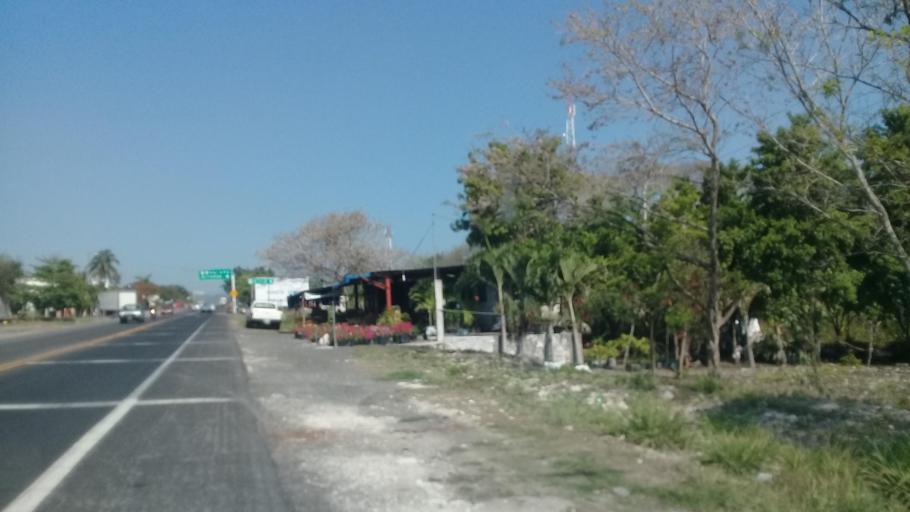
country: MX
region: Veracruz
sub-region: Emiliano Zapata
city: Plan del Rio
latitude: 19.3932
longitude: -96.6168
